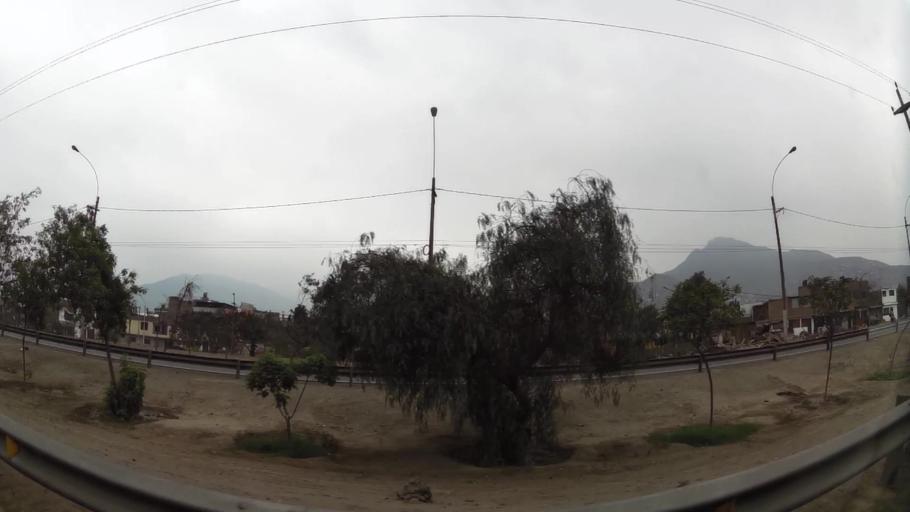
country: PE
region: Lima
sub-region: Lima
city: Vitarte
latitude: -12.0224
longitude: -76.9583
